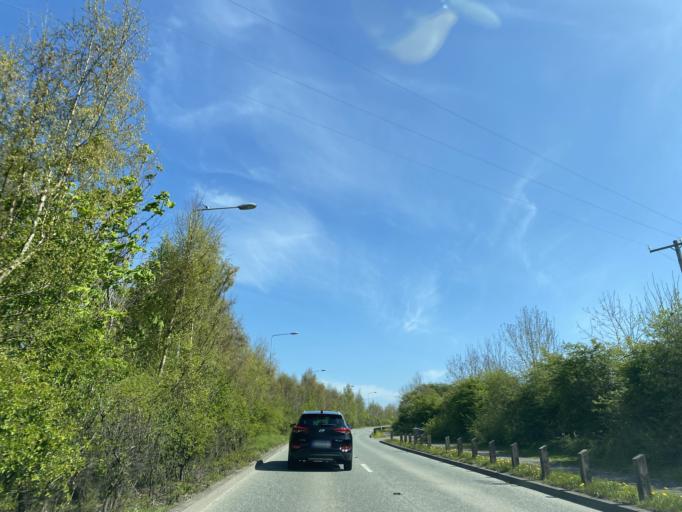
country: IE
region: Leinster
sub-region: Kildare
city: Kill
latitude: 53.2525
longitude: -6.5818
